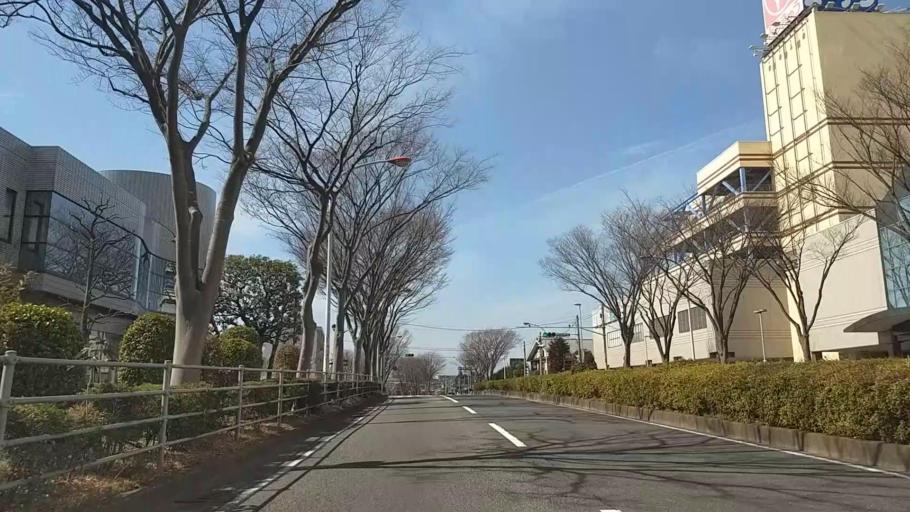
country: JP
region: Kanagawa
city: Fujisawa
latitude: 35.3709
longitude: 139.4420
